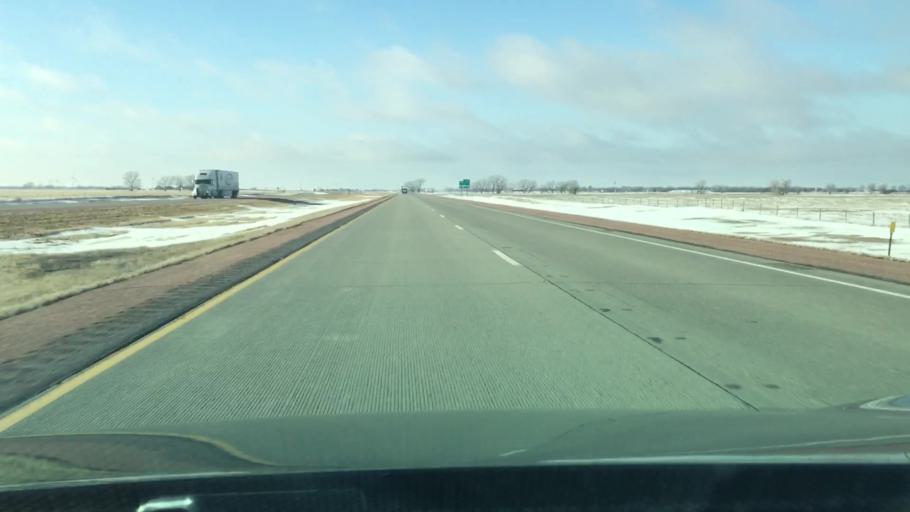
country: US
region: South Dakota
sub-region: Aurora County
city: Plankinton
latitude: 43.7122
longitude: -98.6834
